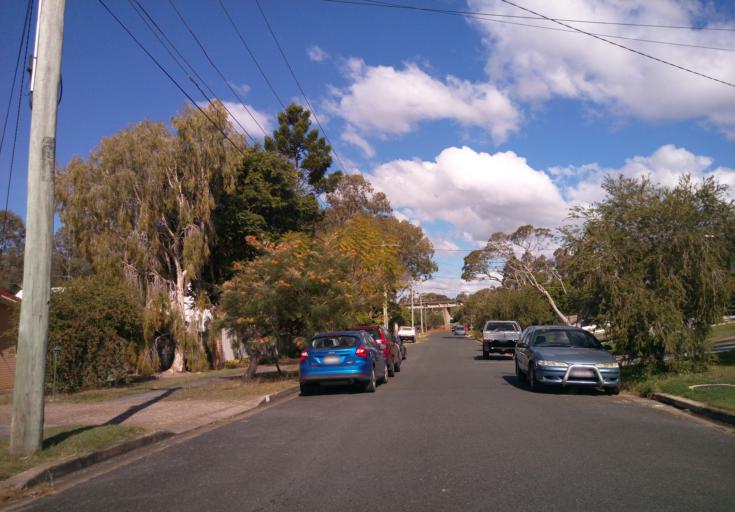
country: AU
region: Queensland
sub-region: Redland
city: Wellington Point
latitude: -27.4914
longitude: 153.2131
